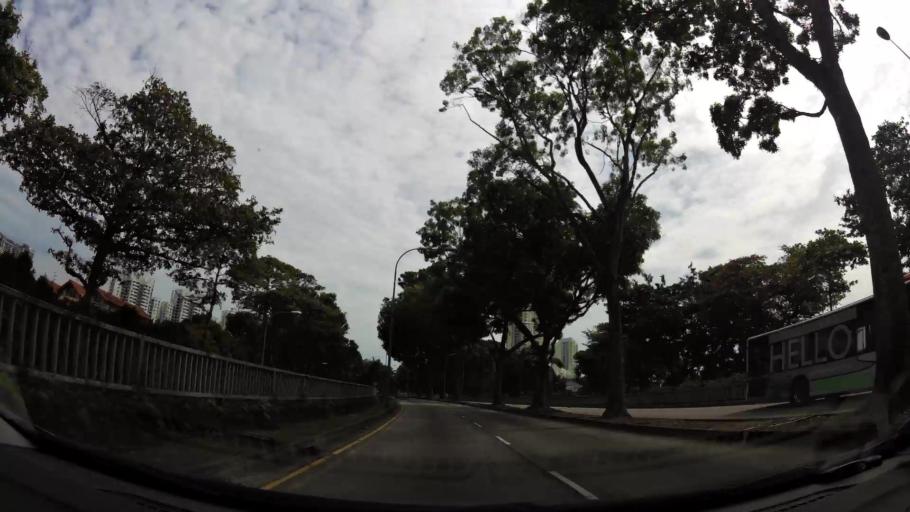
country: SG
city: Singapore
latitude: 1.3076
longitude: 103.7650
